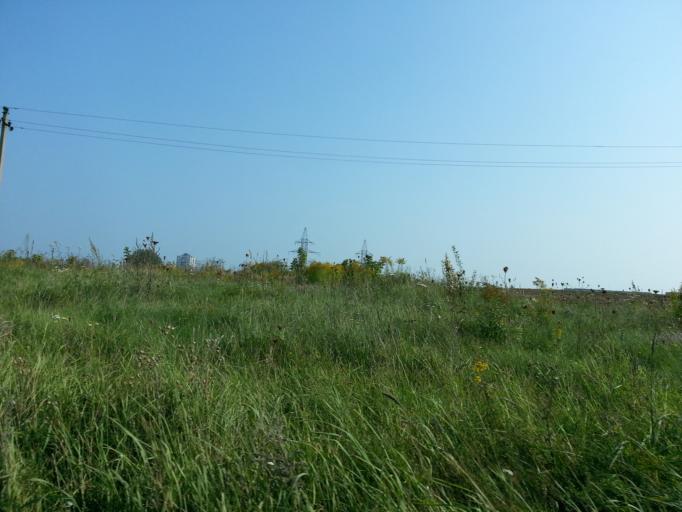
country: LT
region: Vilnius County
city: Justiniskes
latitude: 54.7259
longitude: 25.2060
